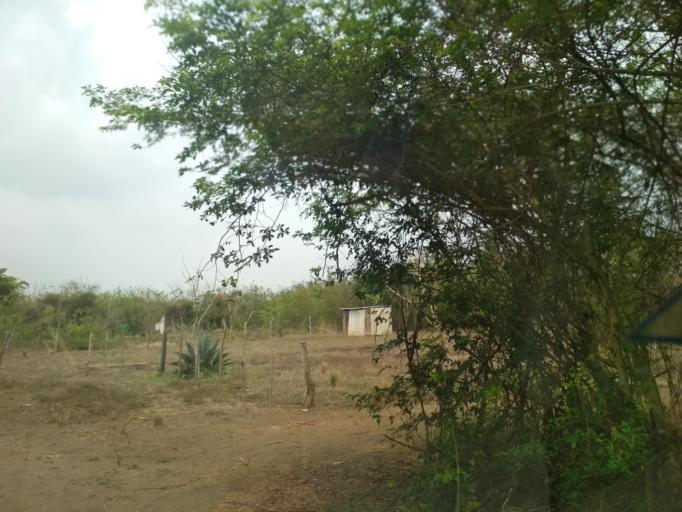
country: MX
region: Veracruz
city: Paso del Toro
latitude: 19.0245
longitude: -96.1412
